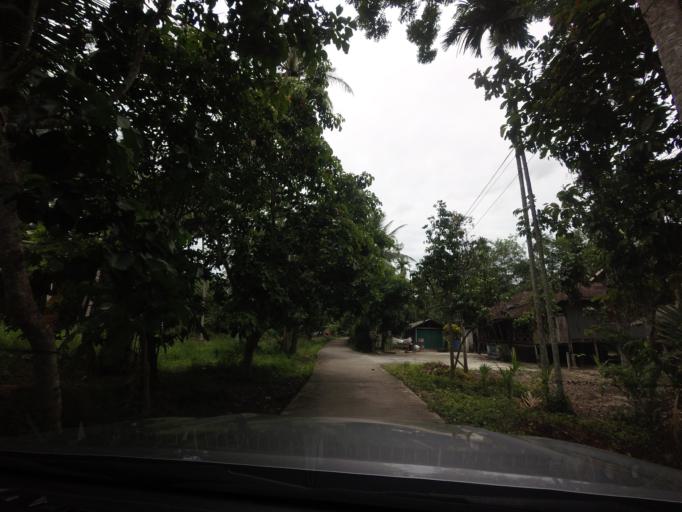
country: TH
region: Pattani
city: Sai Buri
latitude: 6.7039
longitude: 101.5353
